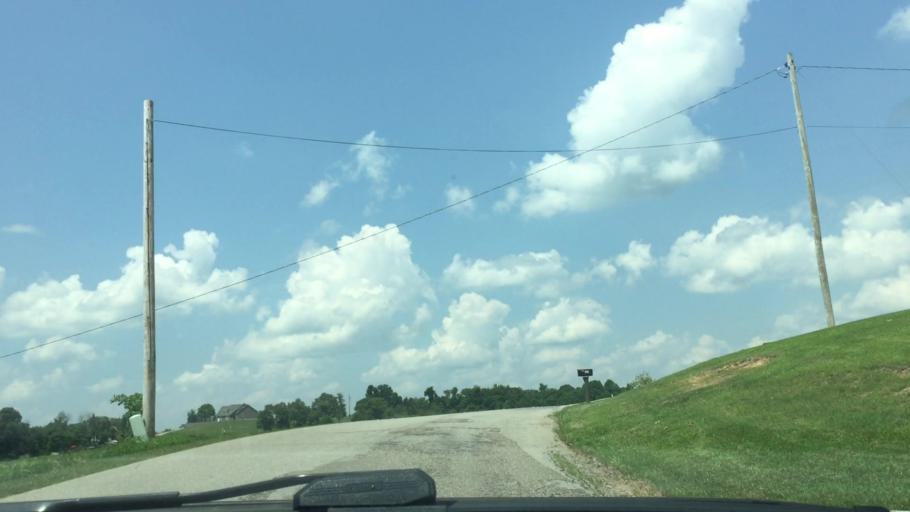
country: US
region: West Virginia
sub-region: Wetzel County
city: New Martinsville
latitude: 39.7068
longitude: -80.7447
